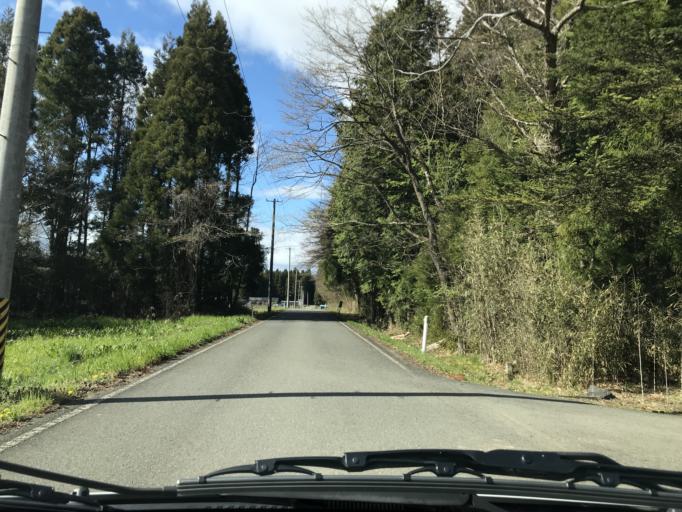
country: JP
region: Iwate
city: Mizusawa
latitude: 39.1066
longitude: 141.0926
